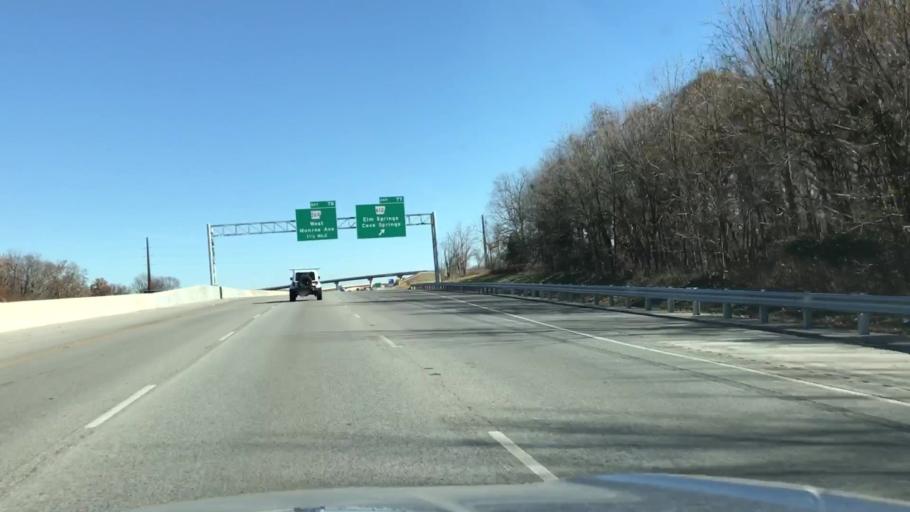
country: US
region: Arkansas
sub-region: Benton County
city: Lowell
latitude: 36.2336
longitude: -94.1701
